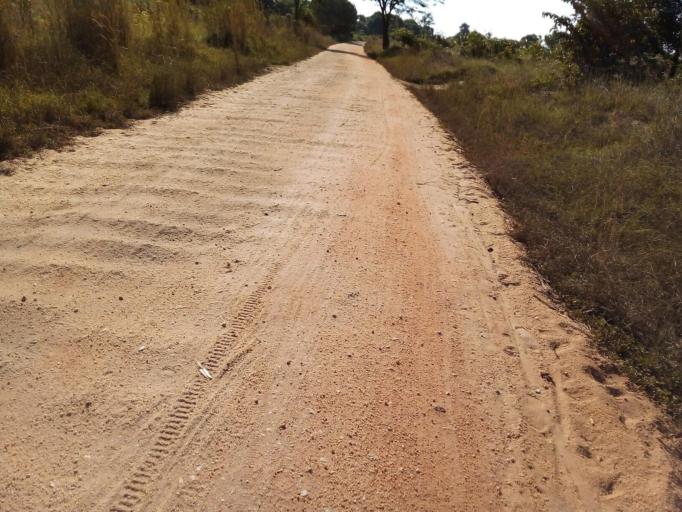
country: MZ
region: Zambezia
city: Quelimane
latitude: -17.5337
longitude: 36.6214
